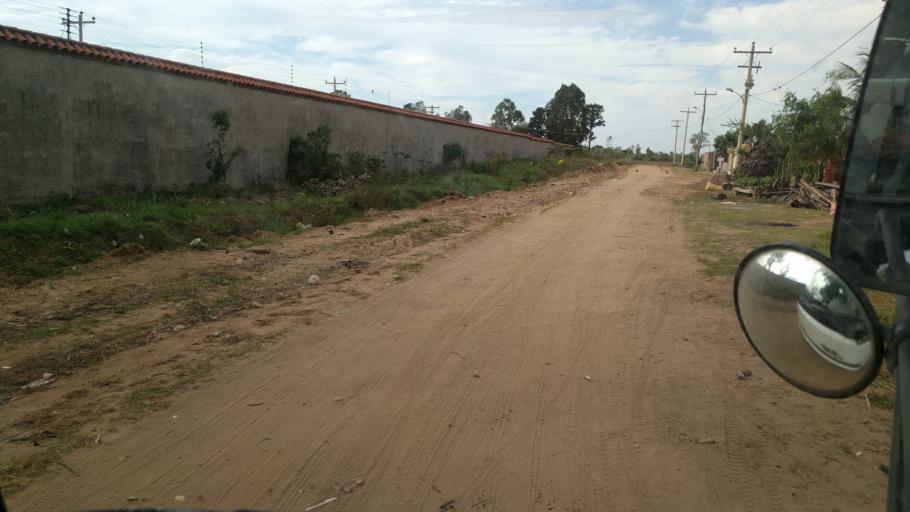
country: BO
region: Santa Cruz
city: Santa Cruz de la Sierra
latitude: -17.6831
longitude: -63.1438
